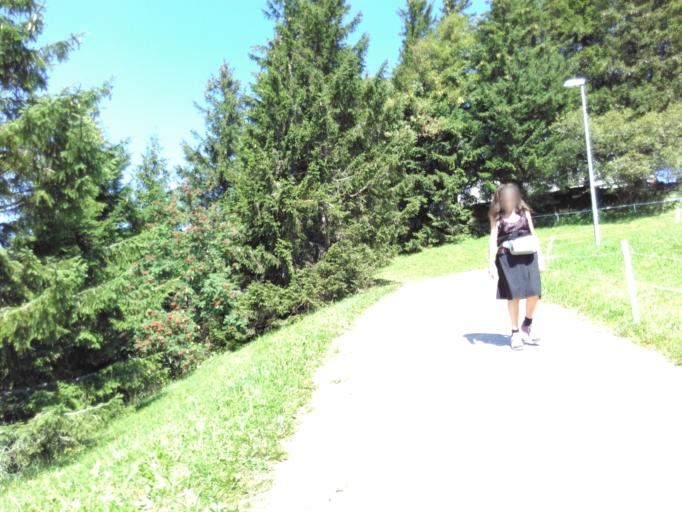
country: CH
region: Lucerne
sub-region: Lucerne-Land District
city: Vitznau
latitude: 47.0539
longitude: 8.4740
